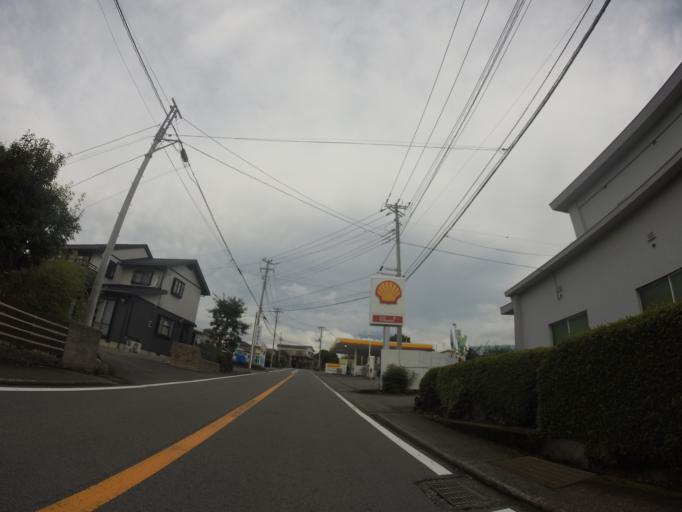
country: JP
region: Shizuoka
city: Fuji
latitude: 35.2167
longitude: 138.6873
